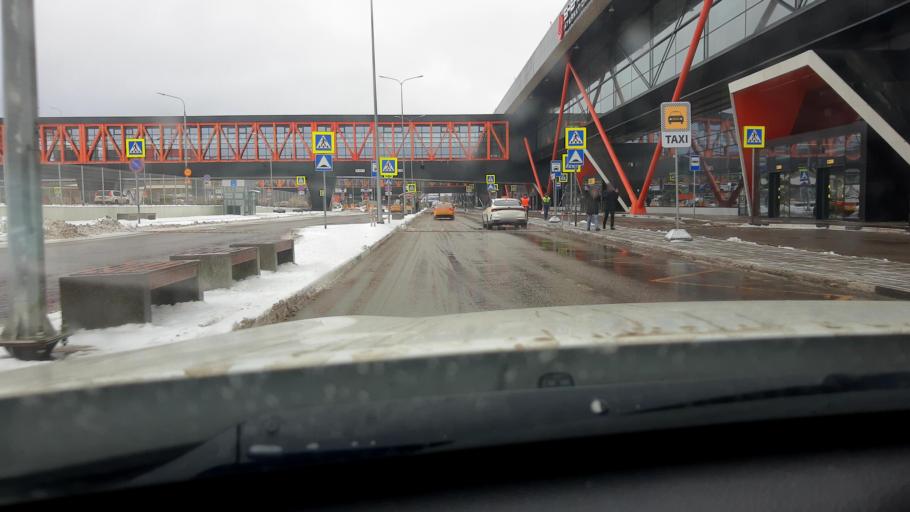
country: RU
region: Moskovskaya
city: Novopodrezkovo
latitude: 55.9808
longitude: 37.4081
